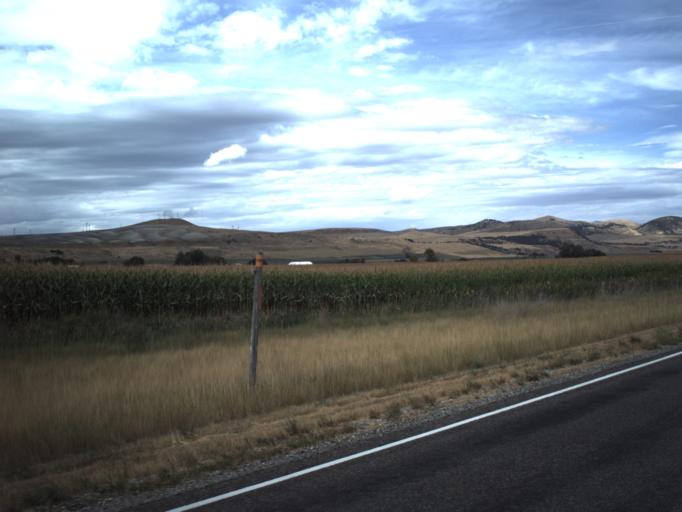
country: US
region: Utah
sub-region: Cache County
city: Lewiston
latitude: 41.9207
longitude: -111.9529
